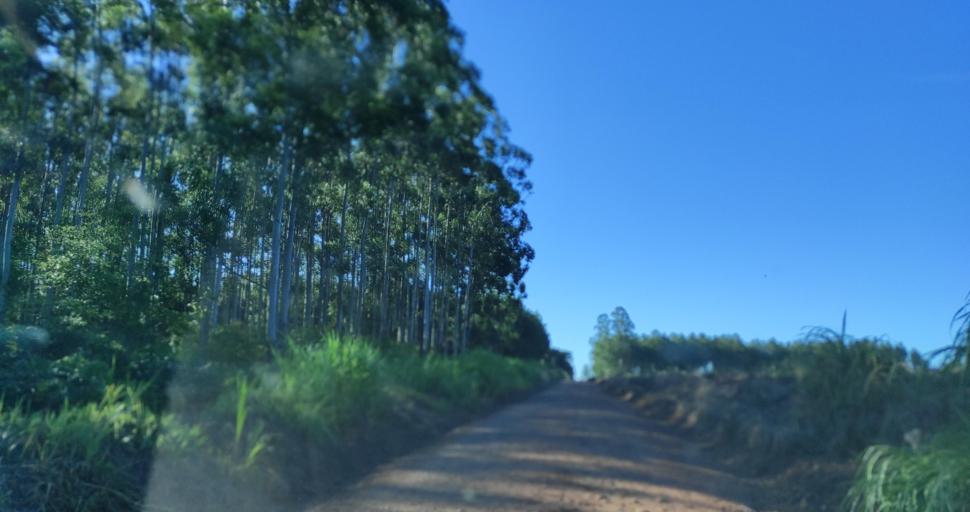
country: AR
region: Misiones
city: Capiovi
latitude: -26.8876
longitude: -54.9970
